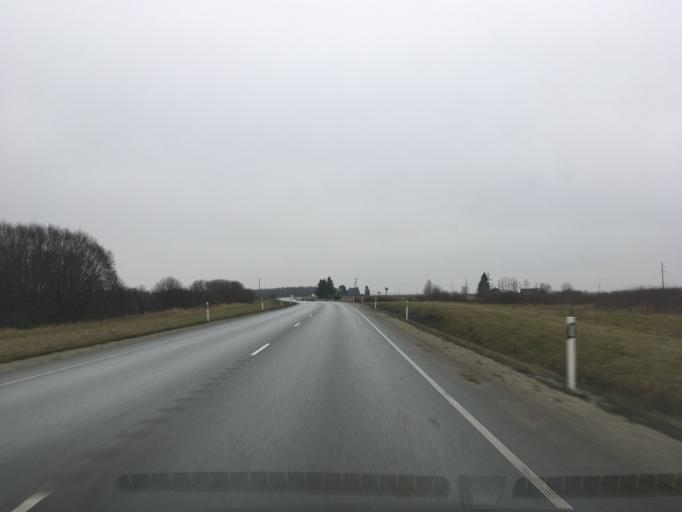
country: EE
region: Ida-Virumaa
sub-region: Kivioli linn
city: Kivioli
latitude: 59.4241
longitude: 26.9636
